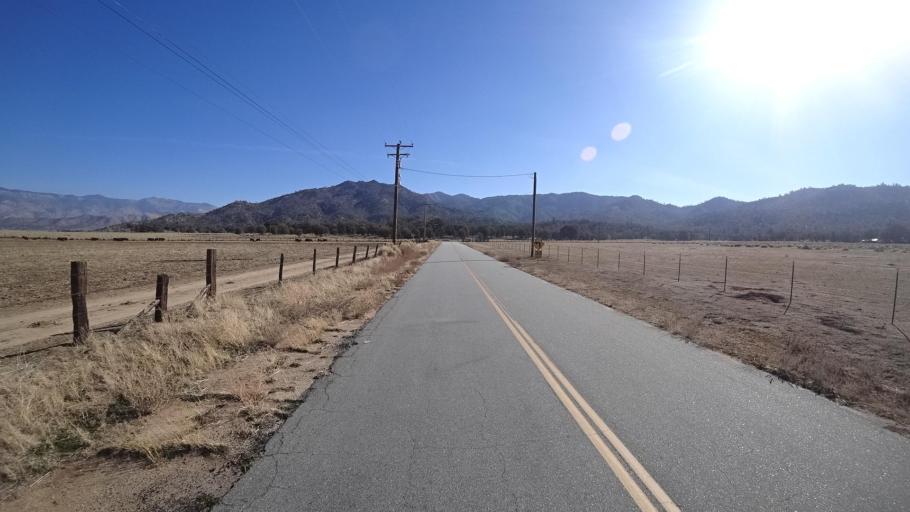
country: US
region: California
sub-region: Kern County
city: Bodfish
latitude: 35.3820
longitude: -118.5474
